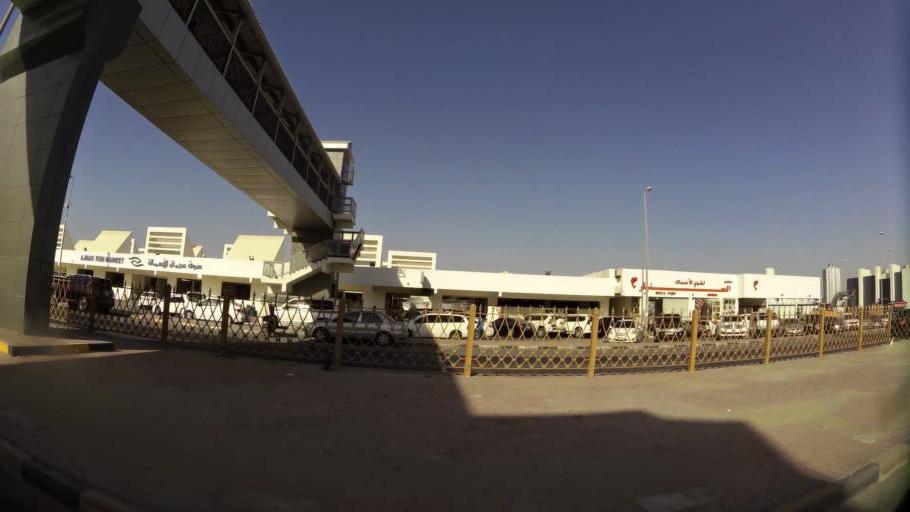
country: AE
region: Ajman
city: Ajman
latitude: 25.4000
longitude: 55.4530
